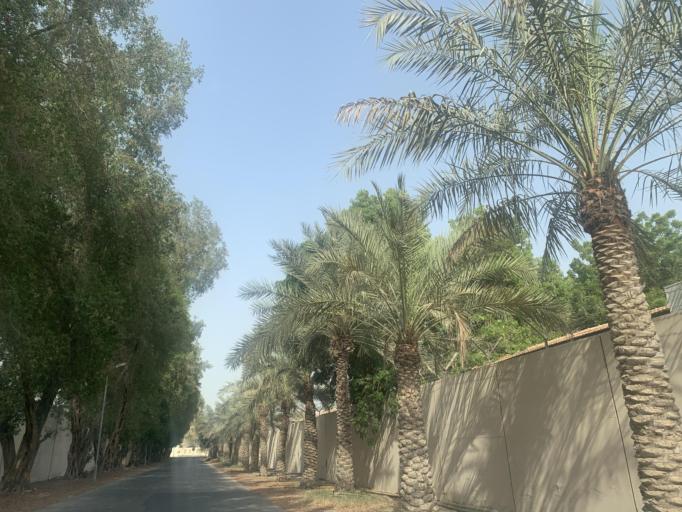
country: BH
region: Manama
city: Jidd Hafs
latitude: 26.2129
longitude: 50.4722
